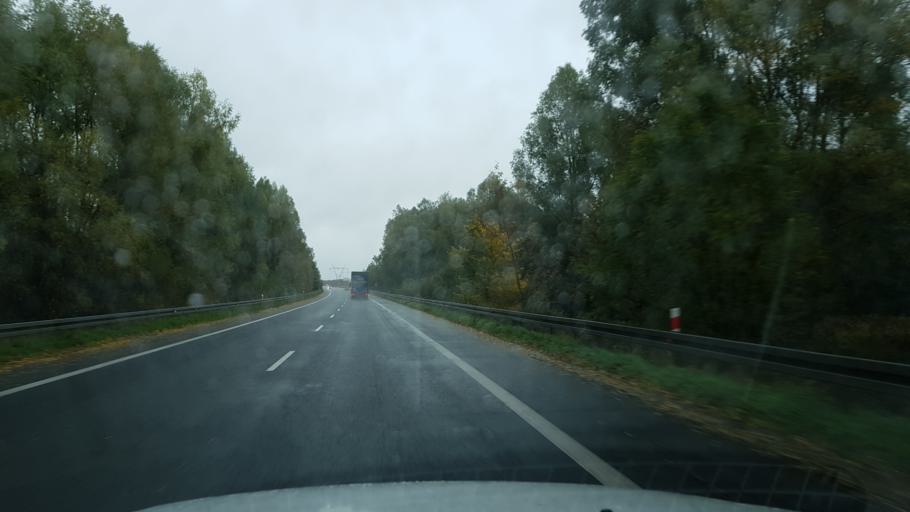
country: PL
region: West Pomeranian Voivodeship
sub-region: Powiat gryfinski
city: Stare Czarnowo
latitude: 53.2828
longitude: 14.7858
